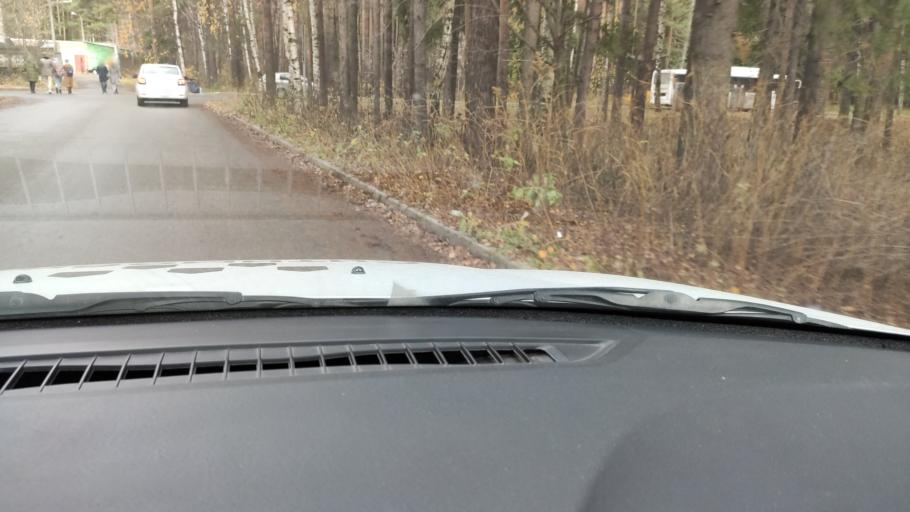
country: RU
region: Perm
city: Perm
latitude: 58.0513
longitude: 56.2185
